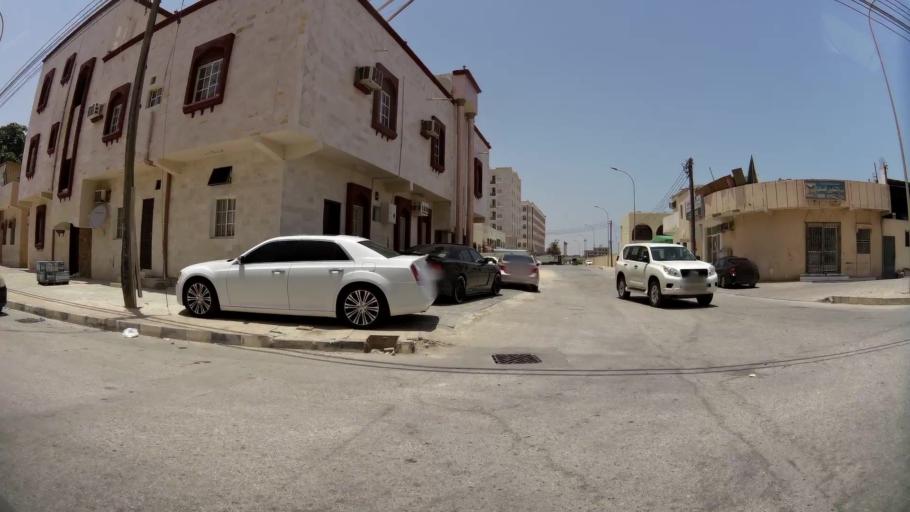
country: OM
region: Zufar
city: Salalah
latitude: 17.0182
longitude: 54.1084
